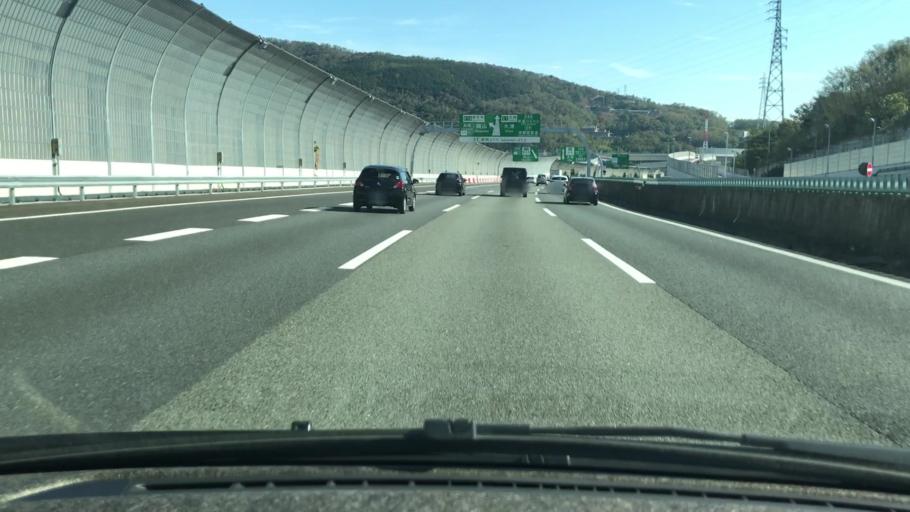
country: JP
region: Osaka
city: Takatsuki
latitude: 34.8678
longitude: 135.6200
